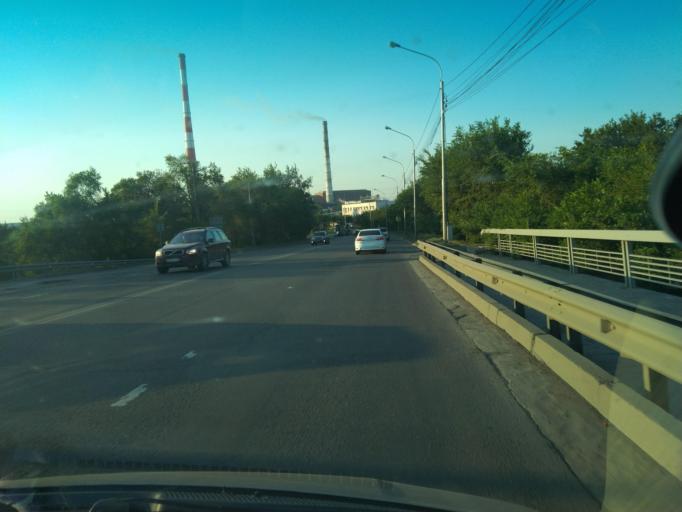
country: RU
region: Krasnoyarskiy
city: Berezovka
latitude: 56.0164
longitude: 93.0314
